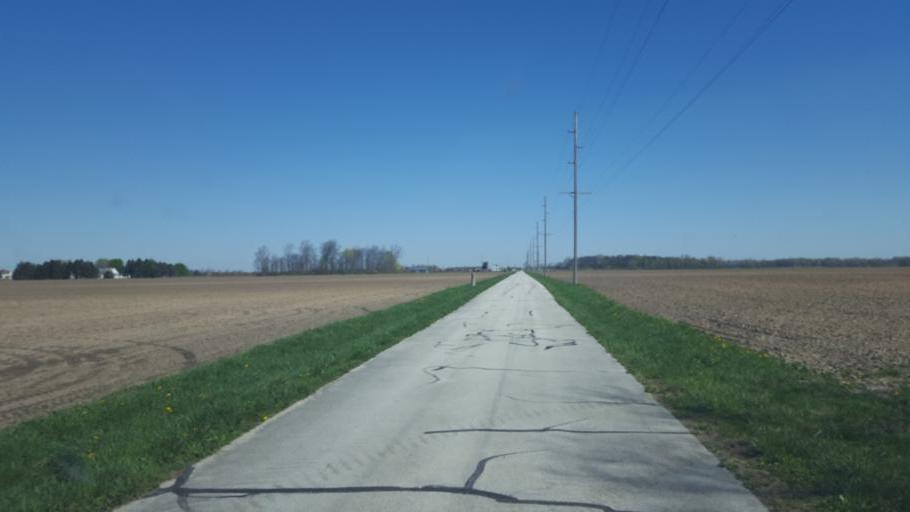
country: US
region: Ohio
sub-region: Seneca County
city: Tiffin
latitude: 41.2198
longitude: -83.1868
